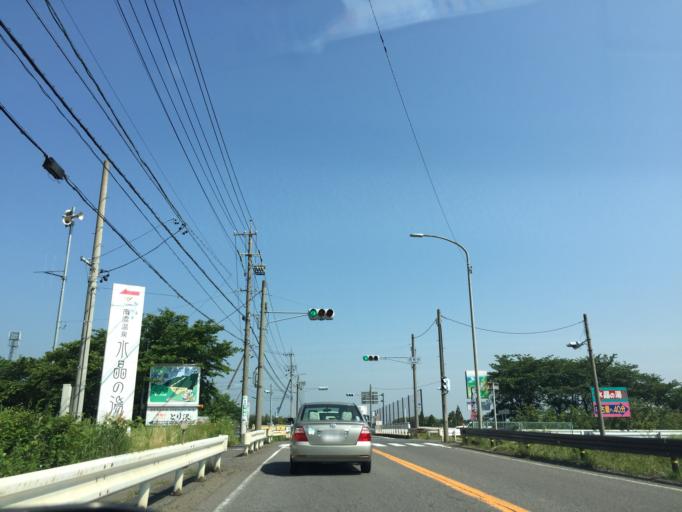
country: JP
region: Aichi
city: Sobue
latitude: 35.2173
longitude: 136.5999
